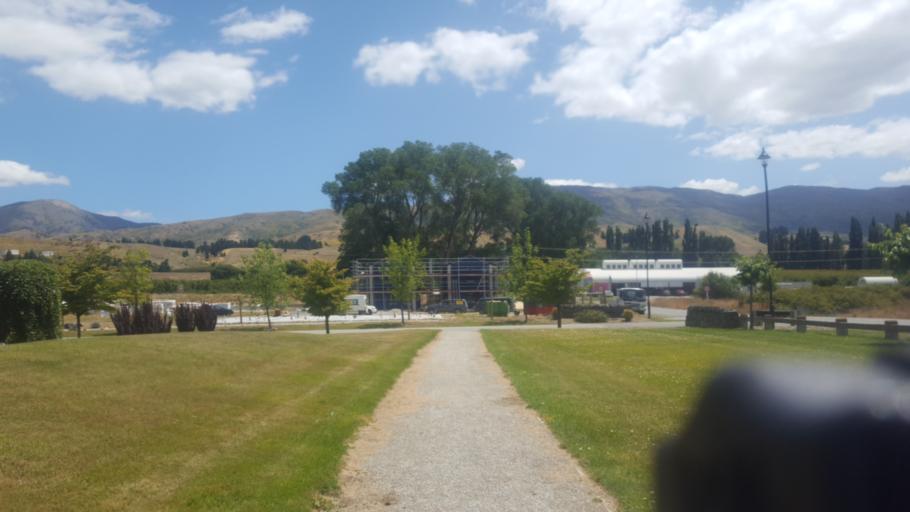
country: NZ
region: Otago
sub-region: Queenstown-Lakes District
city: Wanaka
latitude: -45.0299
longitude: 169.1994
